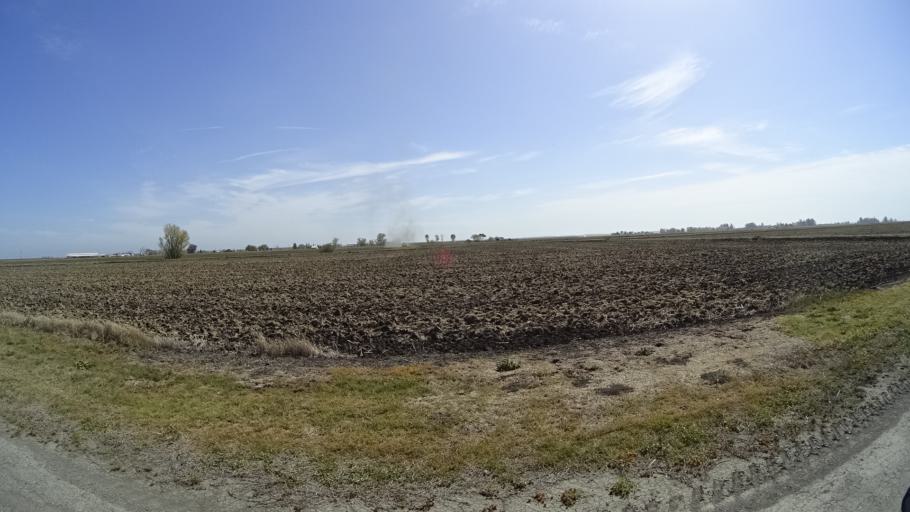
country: US
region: California
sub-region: Glenn County
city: Hamilton City
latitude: 39.6132
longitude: -122.0744
